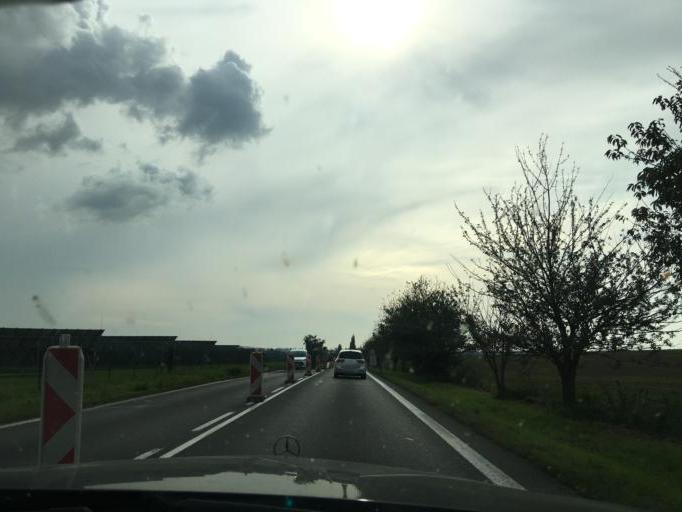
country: CZ
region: Kralovehradecky
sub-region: Okres Hradec Kralove
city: Smirice
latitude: 50.2983
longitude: 15.8448
